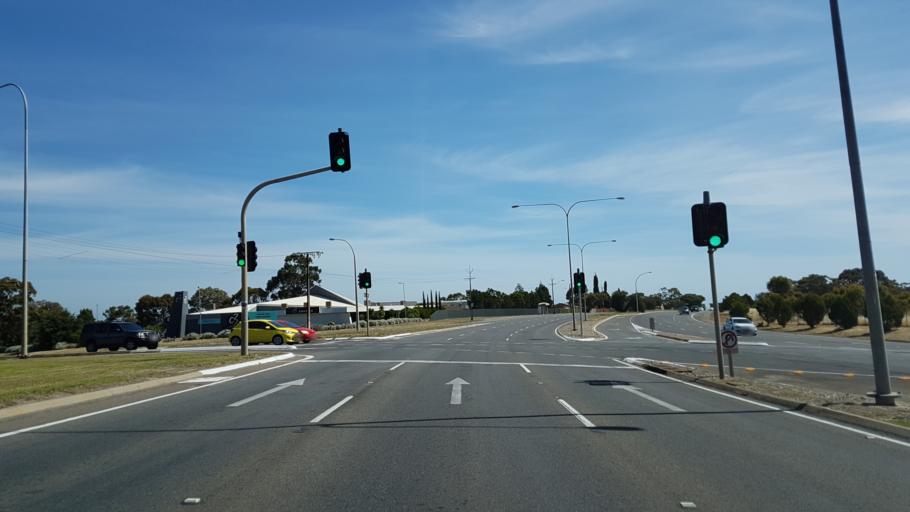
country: AU
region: South Australia
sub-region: Marion
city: Trott Park
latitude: -35.0603
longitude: 138.5596
